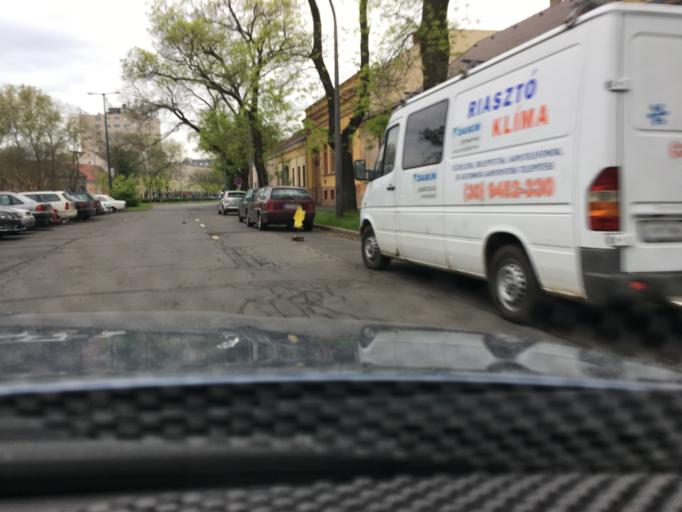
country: HU
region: Hajdu-Bihar
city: Debrecen
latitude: 47.5309
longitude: 21.6354
